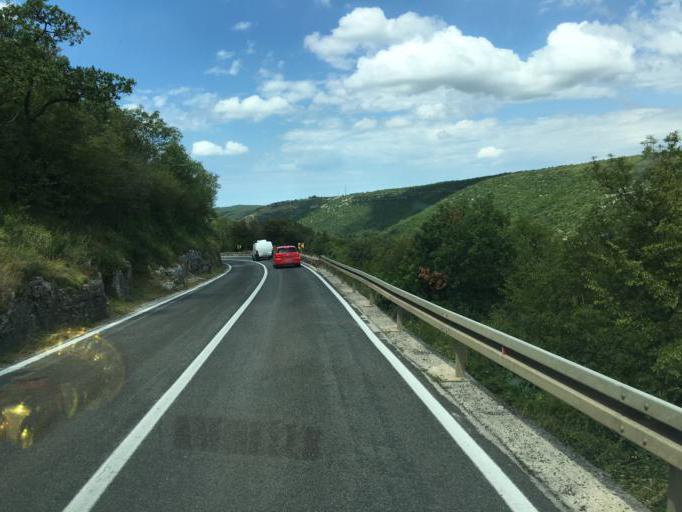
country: HR
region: Istarska
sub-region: Grad Rovinj
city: Rovinj
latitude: 45.1193
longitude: 13.7601
